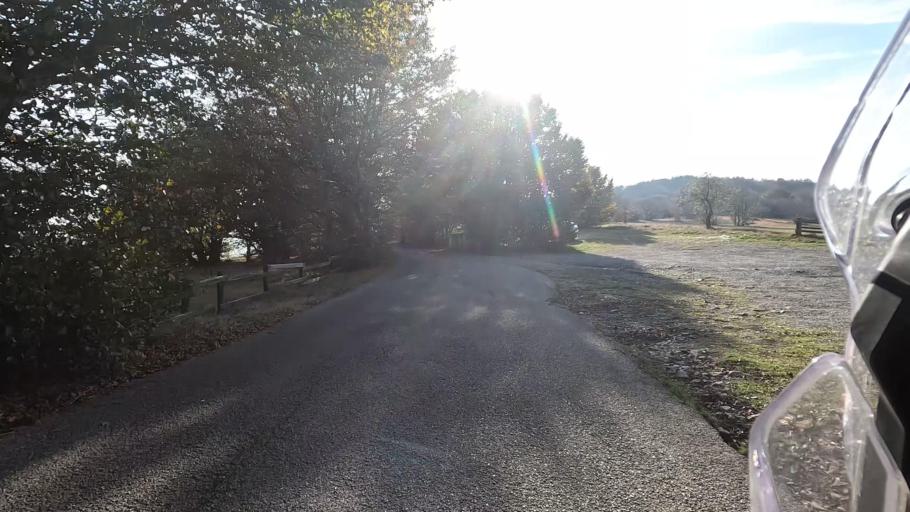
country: IT
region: Liguria
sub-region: Provincia di Savona
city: Urbe
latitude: 44.4323
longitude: 8.5595
